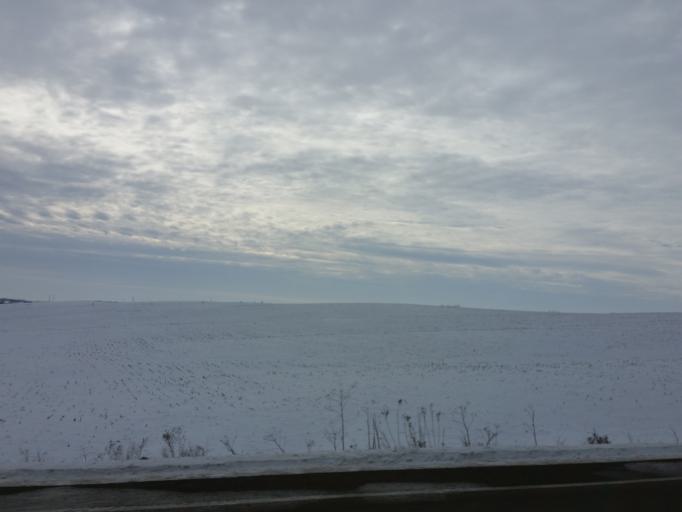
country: US
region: Iowa
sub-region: Dubuque County
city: Peosta
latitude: 42.3821
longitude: -90.7595
